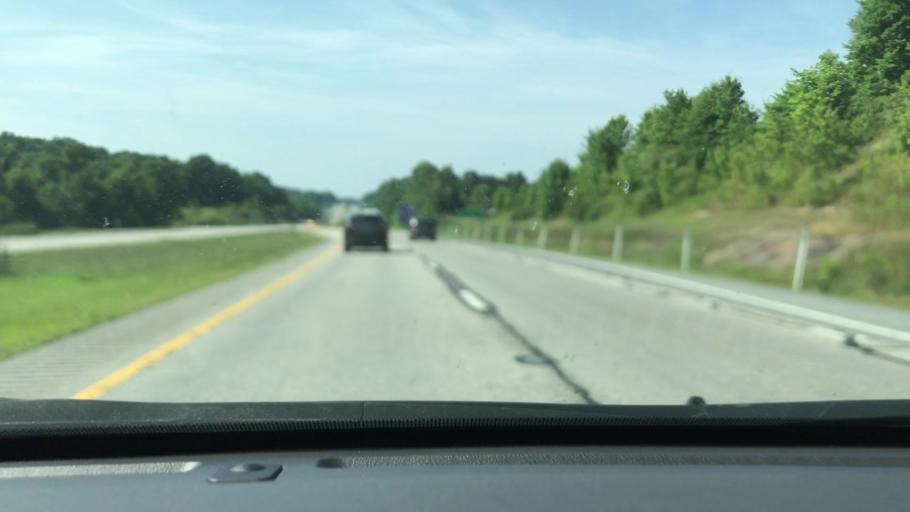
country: US
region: West Virginia
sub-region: Fayette County
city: Fayetteville
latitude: 38.0412
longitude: -81.1229
